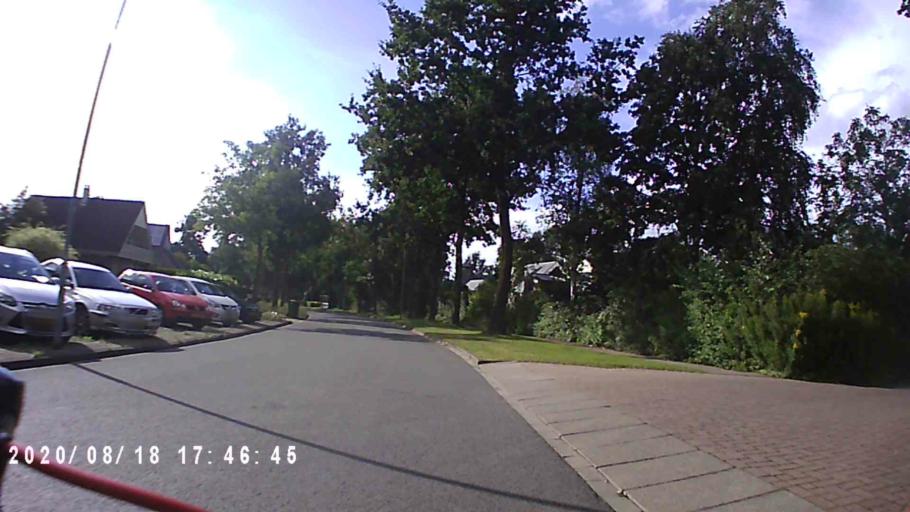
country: NL
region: Groningen
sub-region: Gemeente Zuidhorn
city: Zuidhorn
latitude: 53.2414
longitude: 6.3991
